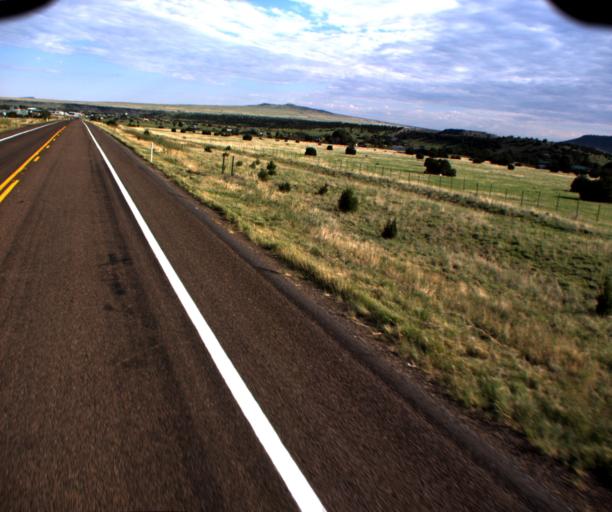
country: US
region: Arizona
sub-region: Apache County
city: Eagar
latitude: 34.0964
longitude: -109.2443
